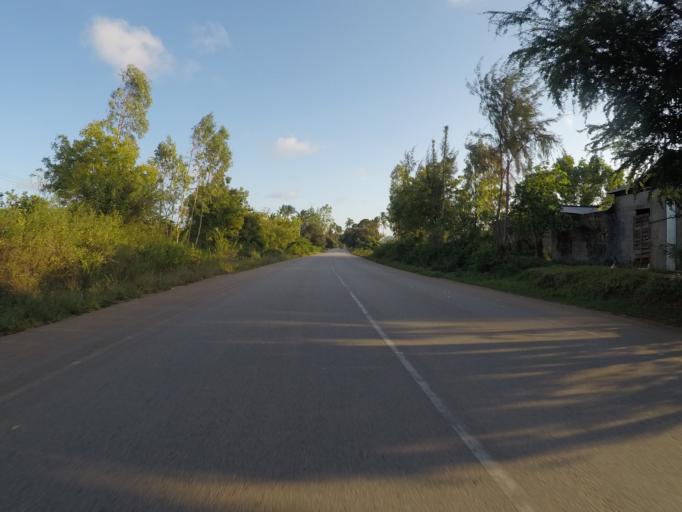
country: TZ
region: Zanzibar North
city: Kijini
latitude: -5.8473
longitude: 39.2838
